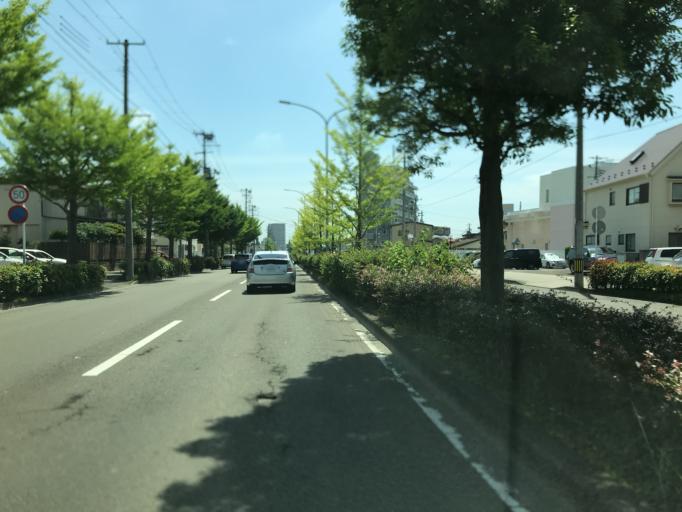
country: JP
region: Miyagi
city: Sendai-shi
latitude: 38.2738
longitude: 140.8871
